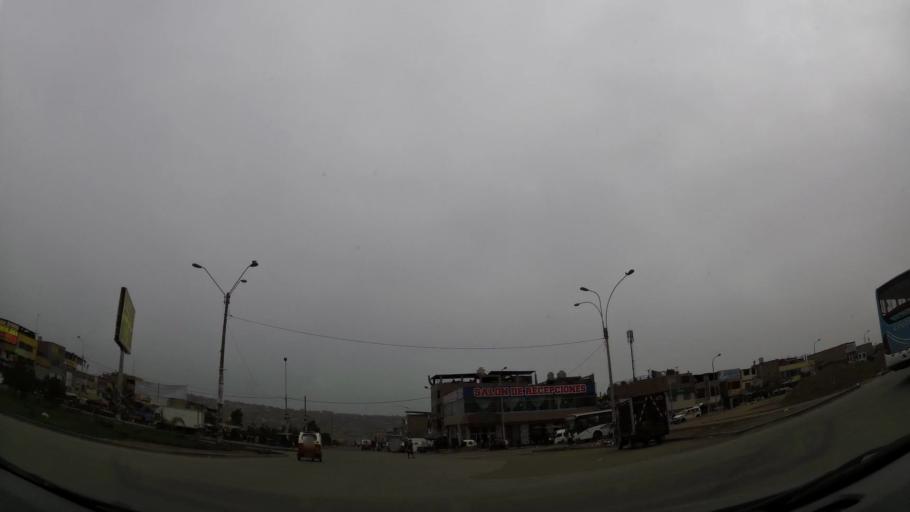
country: PE
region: Lima
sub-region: Lima
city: Surco
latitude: -12.2257
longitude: -76.9408
